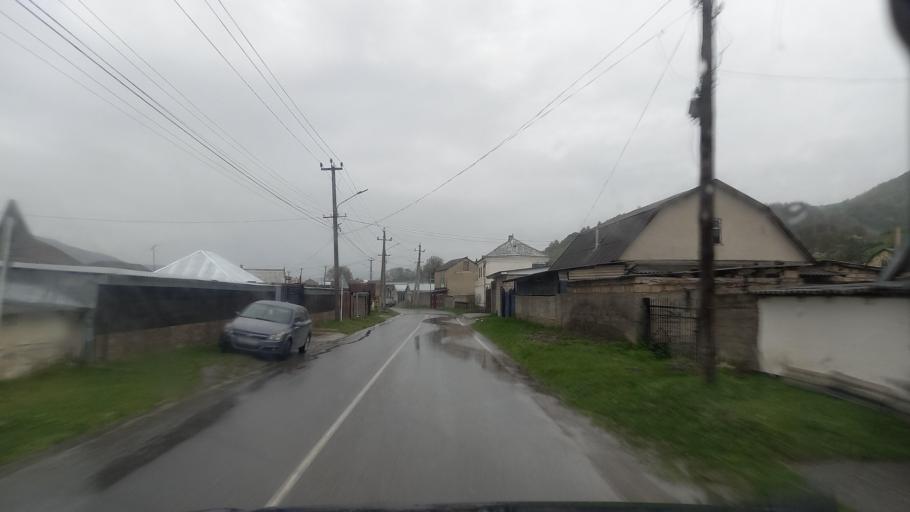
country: RU
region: Kabardino-Balkariya
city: Gundelen
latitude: 43.5952
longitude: 43.1689
